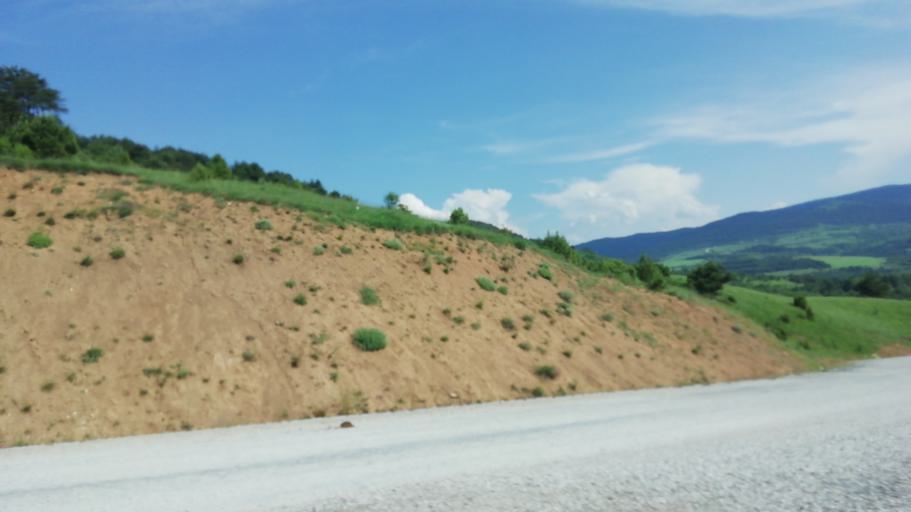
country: TR
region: Karabuk
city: Karabuk
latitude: 41.1169
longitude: 32.5788
